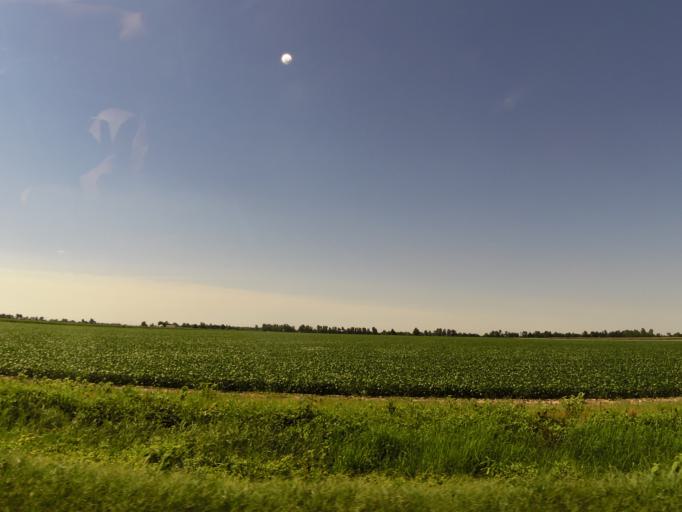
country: US
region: Arkansas
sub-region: Clay County
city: Piggott
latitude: 36.3820
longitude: -90.1636
